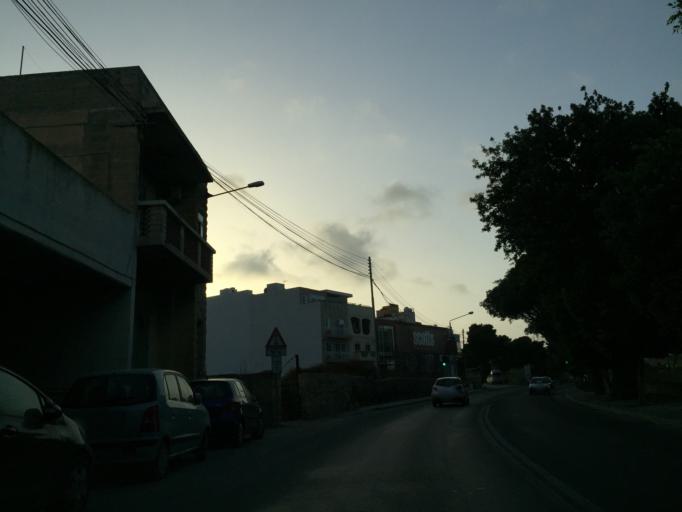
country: MT
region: Saint Paul's Bay
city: San Pawl il-Bahar
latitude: 35.9371
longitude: 14.4123
